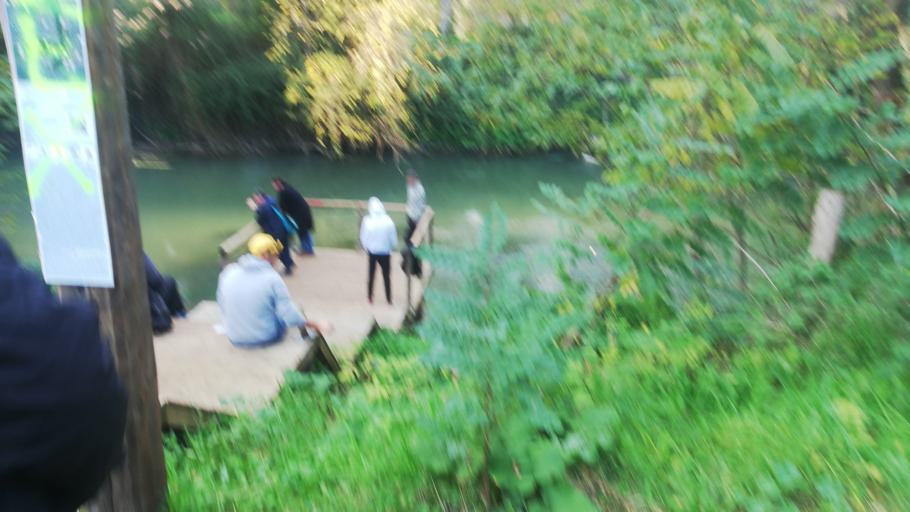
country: IT
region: Latium
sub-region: Citta metropolitana di Roma Capitale
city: Rome
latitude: 41.9321
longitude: 12.5309
